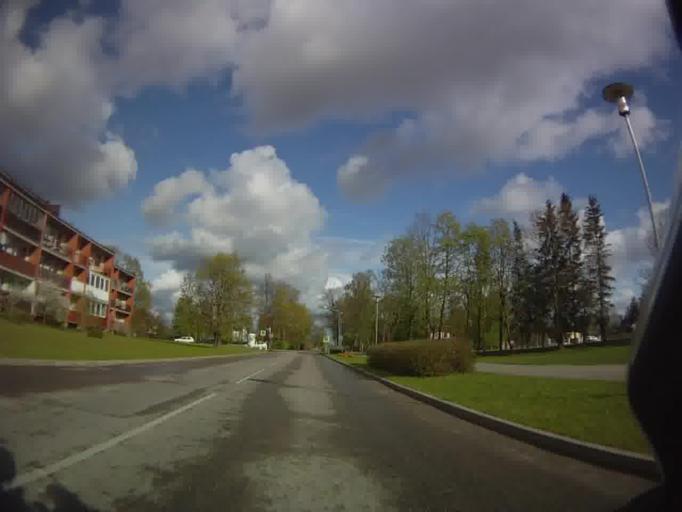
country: LV
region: Sigulda
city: Sigulda
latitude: 57.1618
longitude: 24.8562
